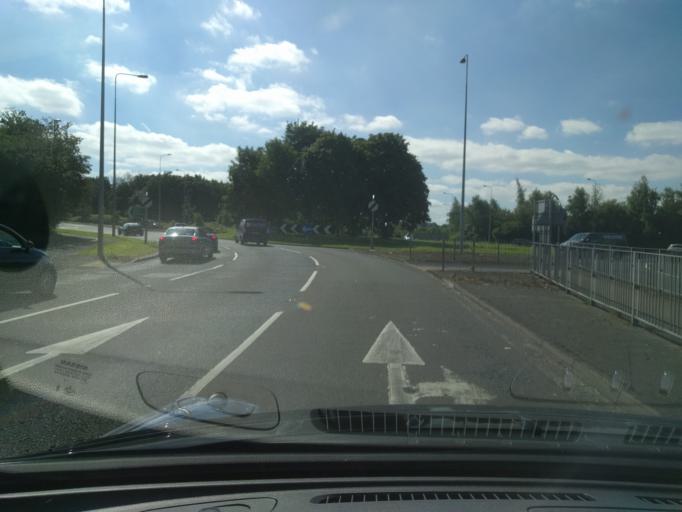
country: GB
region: England
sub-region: Warrington
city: Lymm
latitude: 53.3987
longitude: -2.5126
